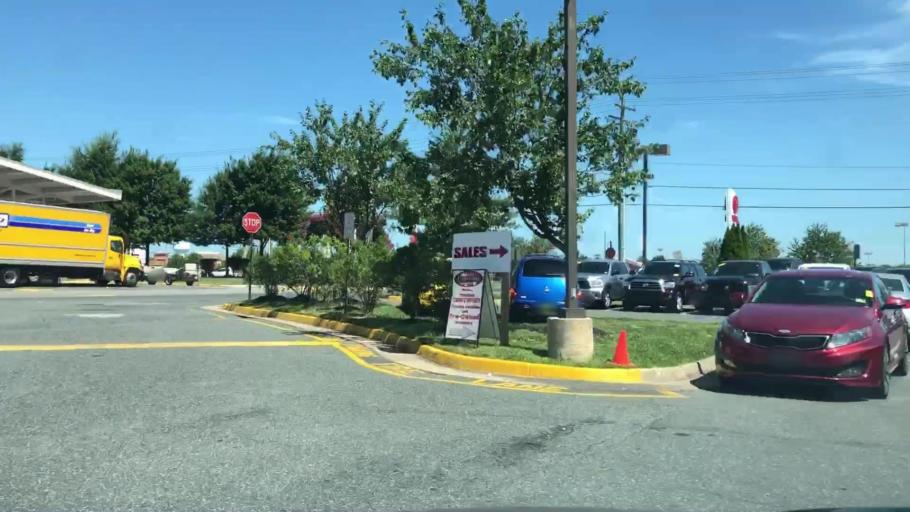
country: US
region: Virginia
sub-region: Stafford County
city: Aquia Harbour
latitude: 38.4669
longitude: -77.4113
